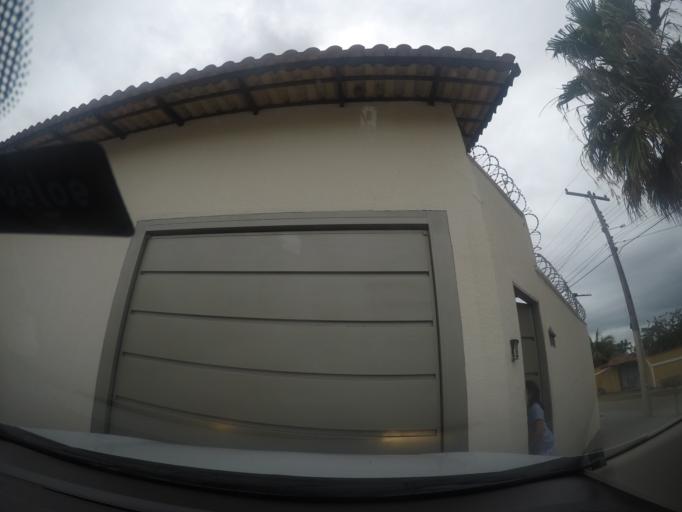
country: BR
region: Goias
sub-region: Goiania
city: Goiania
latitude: -16.7517
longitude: -49.3138
